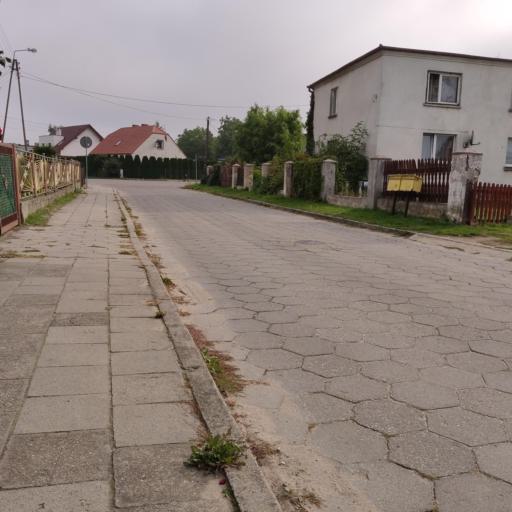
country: PL
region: Kujawsko-Pomorskie
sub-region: Powiat zninski
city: Znin
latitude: 52.8478
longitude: 17.7495
